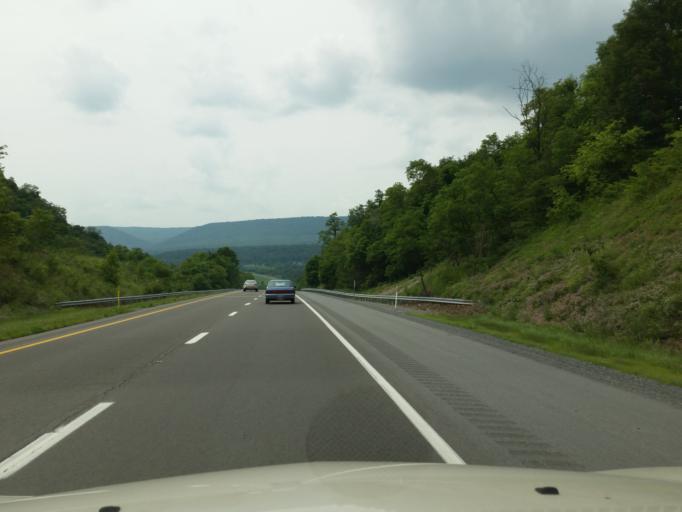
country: US
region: Pennsylvania
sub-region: Juniata County
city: Mifflintown
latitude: 40.5953
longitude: -77.3789
